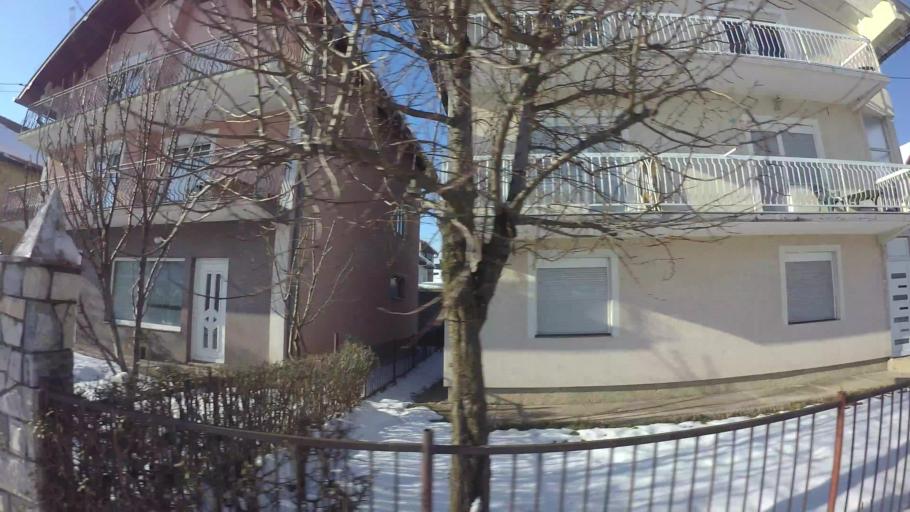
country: BA
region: Federation of Bosnia and Herzegovina
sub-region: Kanton Sarajevo
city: Sarajevo
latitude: 43.8155
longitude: 18.3253
